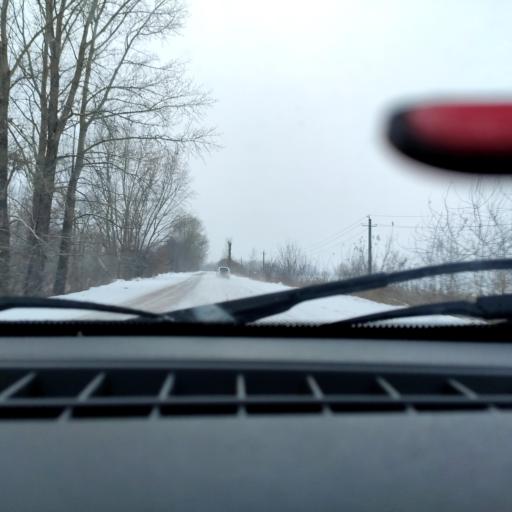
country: RU
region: Bashkortostan
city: Blagoveshchensk
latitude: 54.9108
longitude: 56.0053
